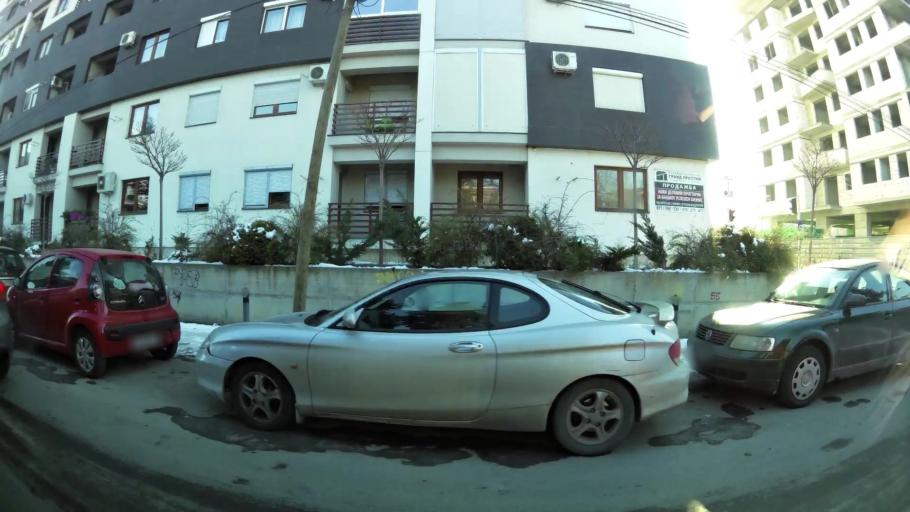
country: MK
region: Karpos
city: Skopje
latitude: 41.9987
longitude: 21.3974
